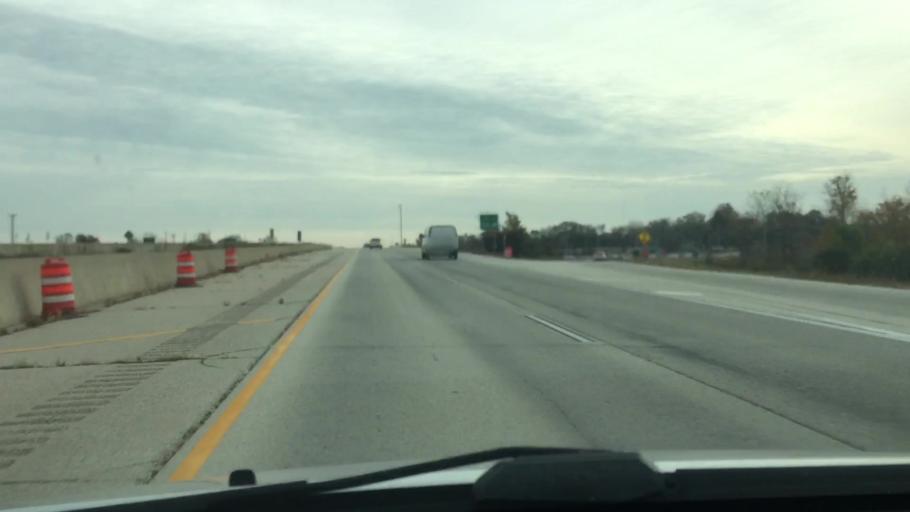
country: US
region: Wisconsin
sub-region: Waukesha County
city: Big Bend
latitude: 42.9102
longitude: -88.2202
